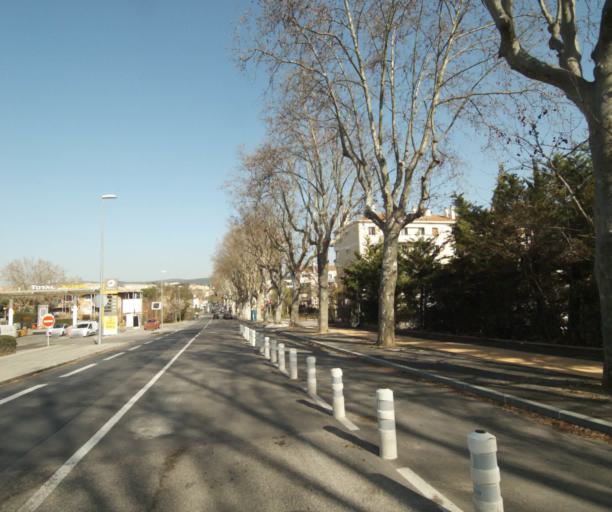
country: FR
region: Provence-Alpes-Cote d'Azur
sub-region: Departement des Bouches-du-Rhone
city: Aix-en-Provence
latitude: 43.5082
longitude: 5.4389
